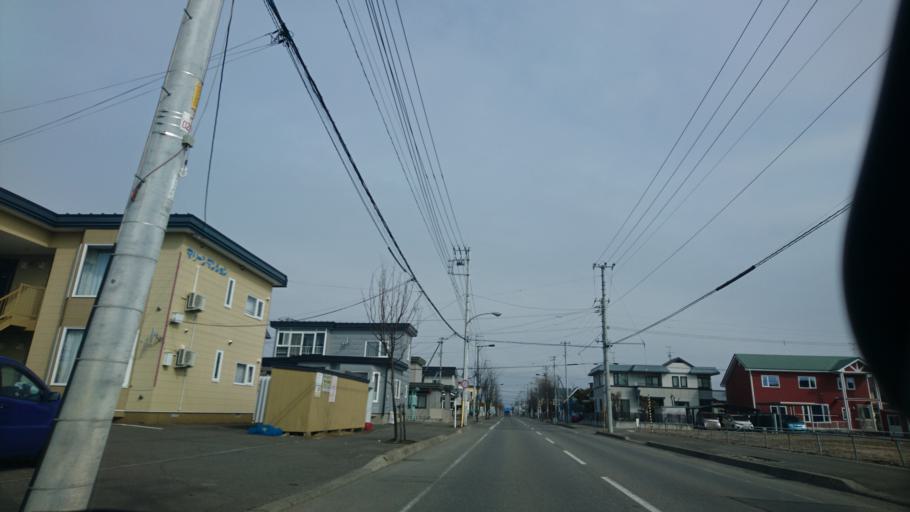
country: JP
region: Hokkaido
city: Otofuke
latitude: 42.9649
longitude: 143.2133
